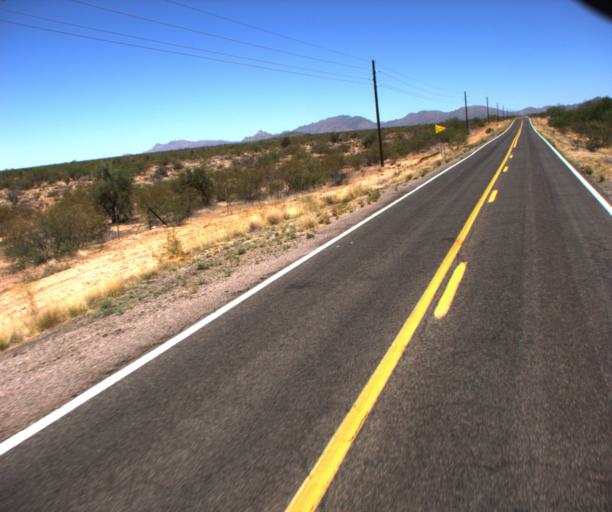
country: US
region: Arizona
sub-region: Yavapai County
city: Congress
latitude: 34.0847
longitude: -112.8256
